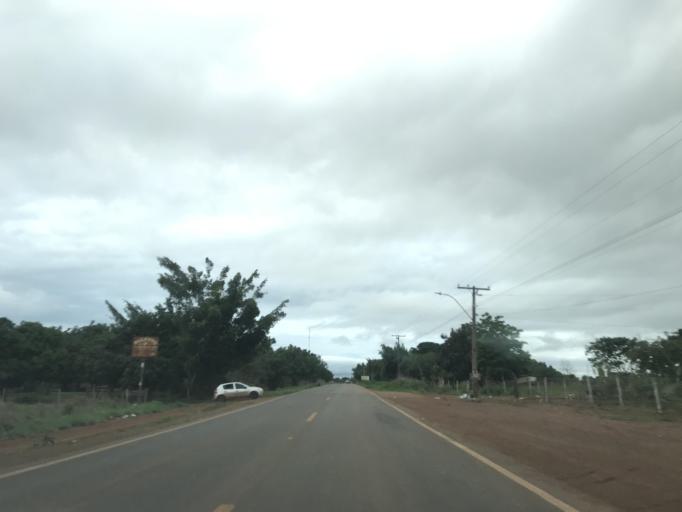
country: BR
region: Goias
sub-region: Luziania
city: Luziania
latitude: -16.3353
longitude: -48.0189
